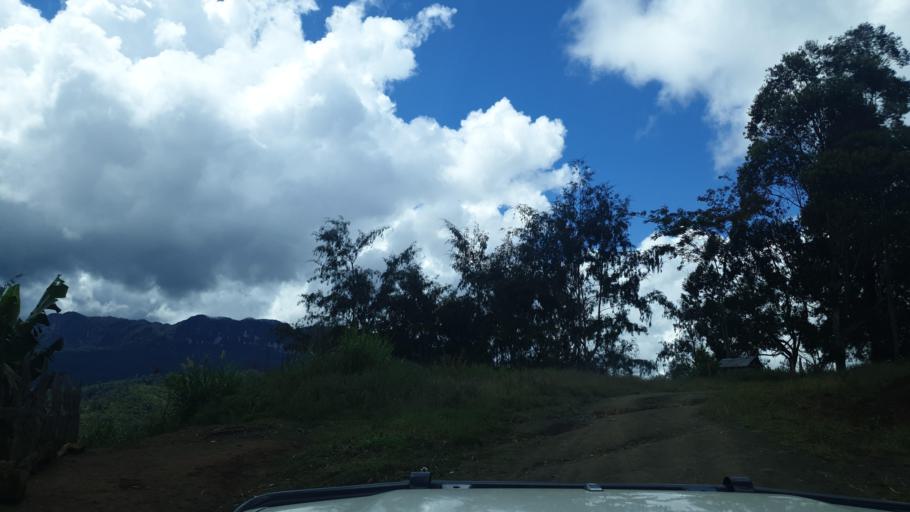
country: PG
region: Eastern Highlands
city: Goroka
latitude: -6.2748
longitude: 145.1890
